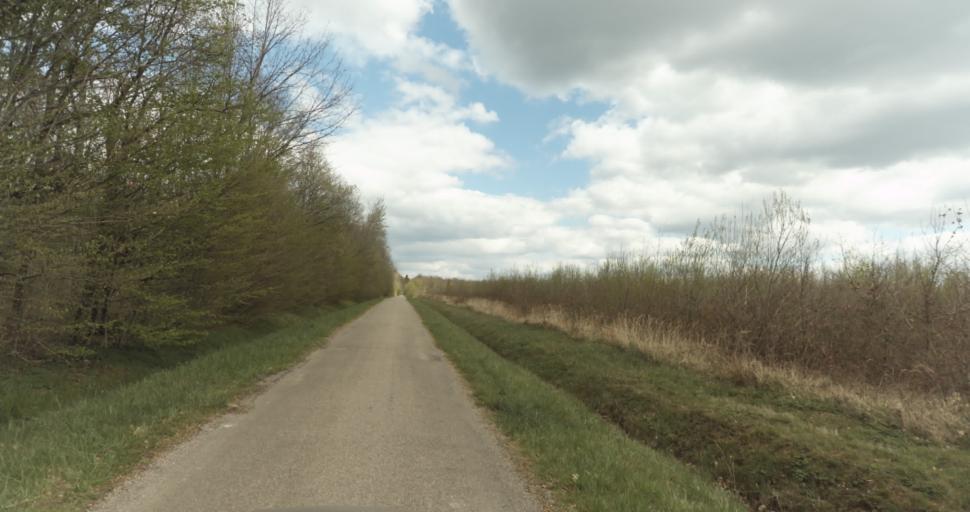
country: FR
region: Franche-Comte
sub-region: Departement du Jura
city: Champvans
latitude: 47.1560
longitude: 5.4335
